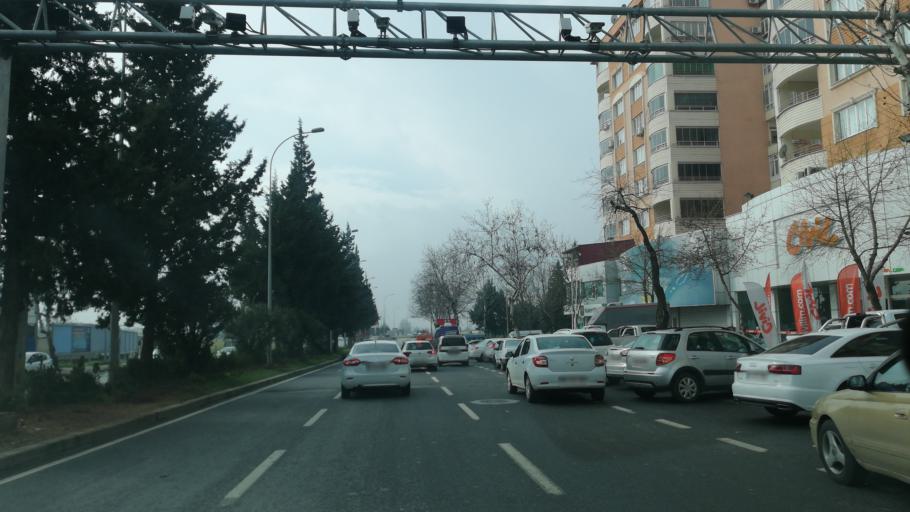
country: TR
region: Kahramanmaras
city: Kahramanmaras
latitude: 37.5705
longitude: 36.9253
